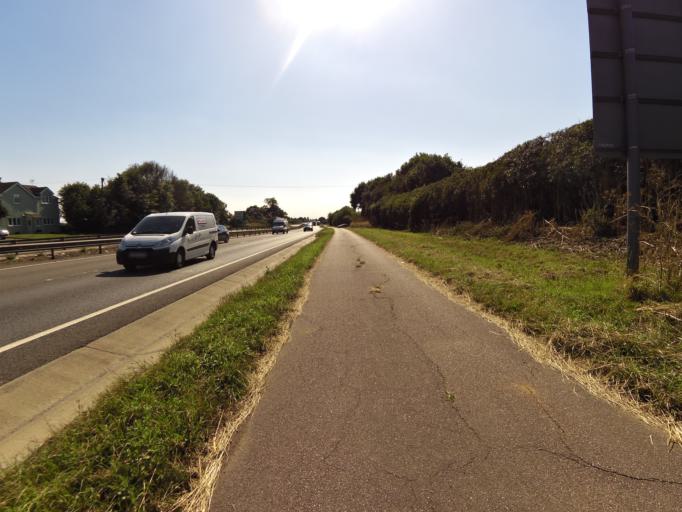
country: GB
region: England
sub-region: Essex
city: Marks Tey
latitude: 51.8553
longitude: 0.7371
